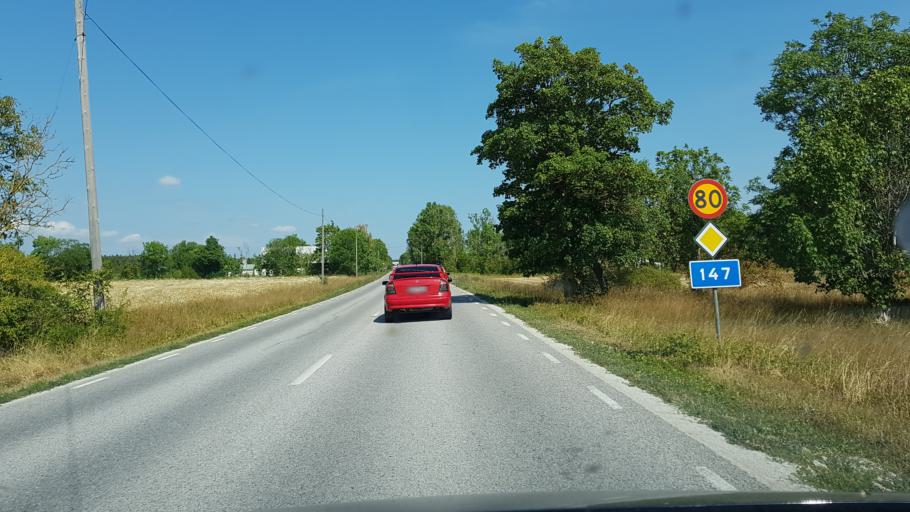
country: SE
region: Gotland
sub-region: Gotland
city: Visby
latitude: 57.6316
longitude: 18.4417
